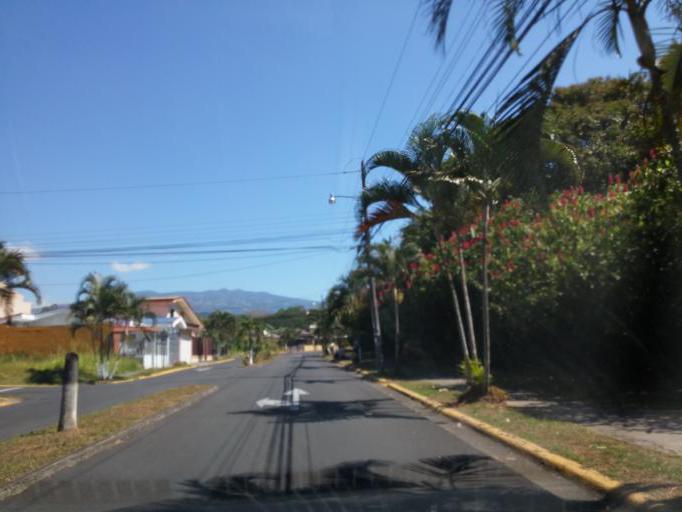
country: CR
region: Alajuela
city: Alajuela
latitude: 10.0168
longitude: -84.1998
